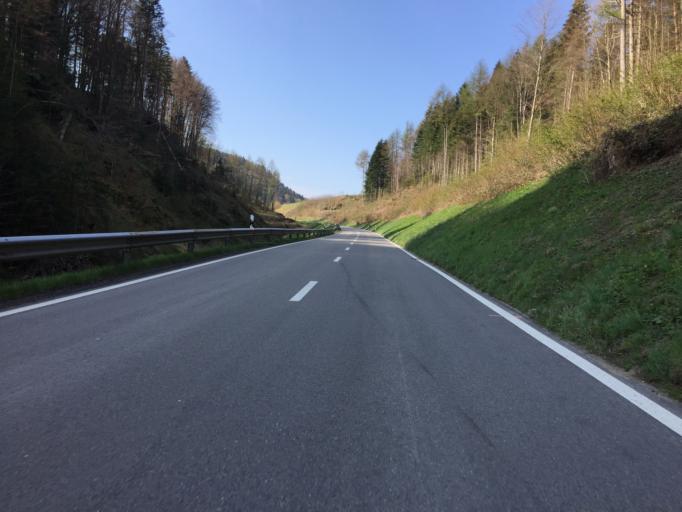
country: CH
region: Bern
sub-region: Bern-Mittelland District
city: Bariswil
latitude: 46.9974
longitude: 7.5230
